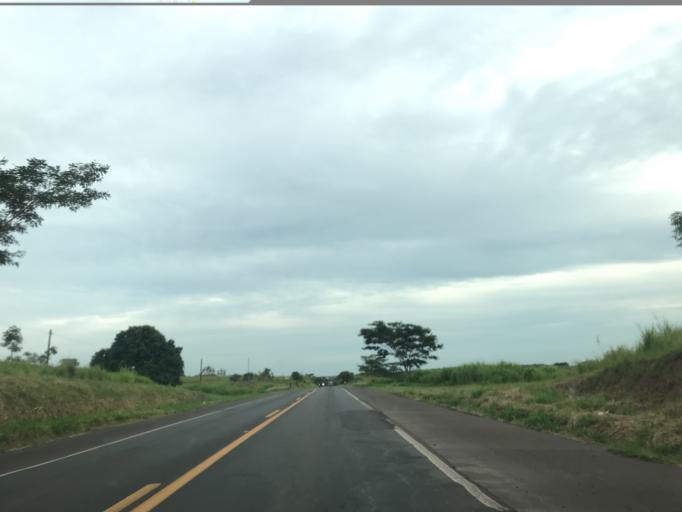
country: BR
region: Sao Paulo
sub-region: Birigui
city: Birigui
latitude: -21.5880
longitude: -50.4581
